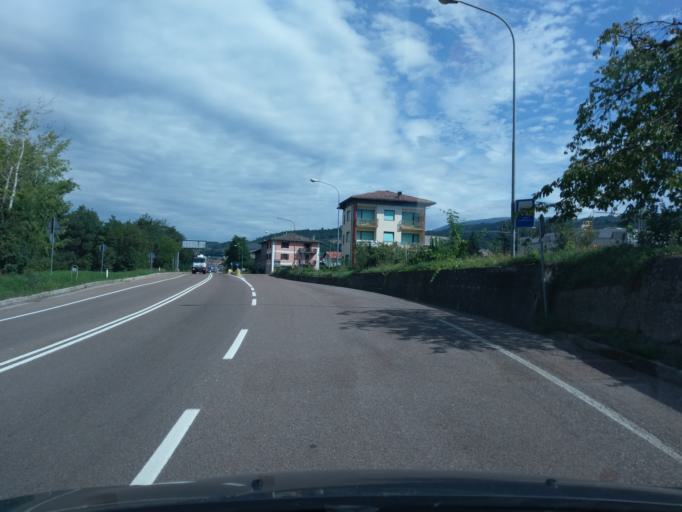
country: IT
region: Trentino-Alto Adige
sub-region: Provincia di Trento
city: Denno
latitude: 46.2933
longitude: 11.0669
